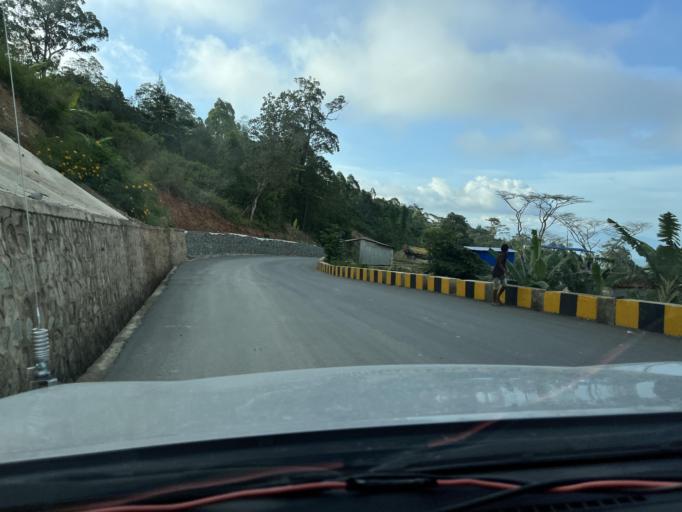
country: TL
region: Dili
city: Dili
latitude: -8.6180
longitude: 125.6385
